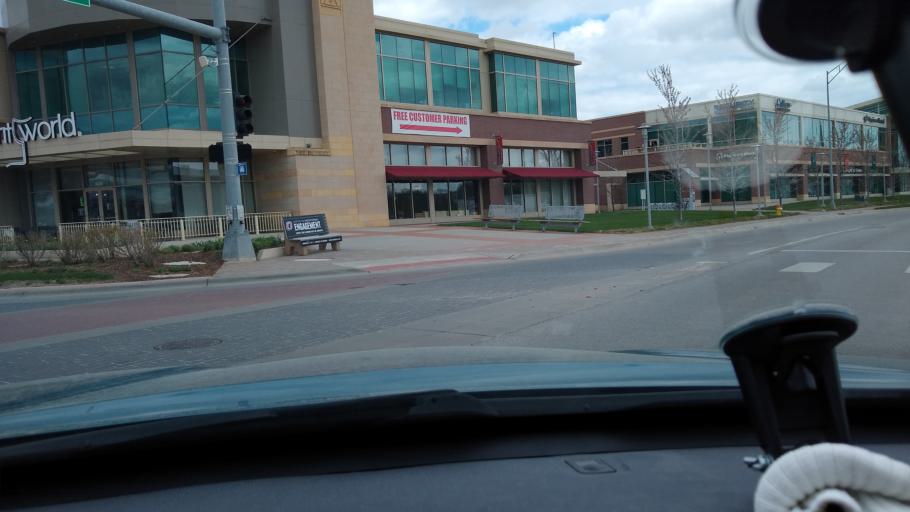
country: US
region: Nebraska
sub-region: Douglas County
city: Ralston
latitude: 41.2378
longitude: -96.0140
